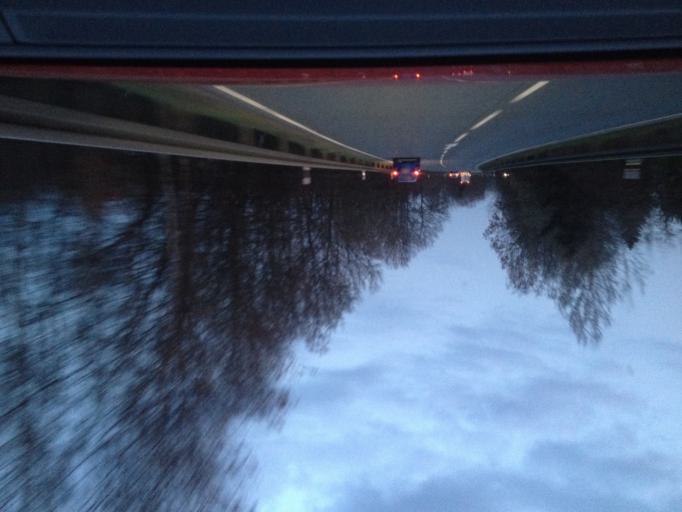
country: DE
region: Bavaria
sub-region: Upper Franconia
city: Marktredwitz
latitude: 50.0127
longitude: 12.0812
